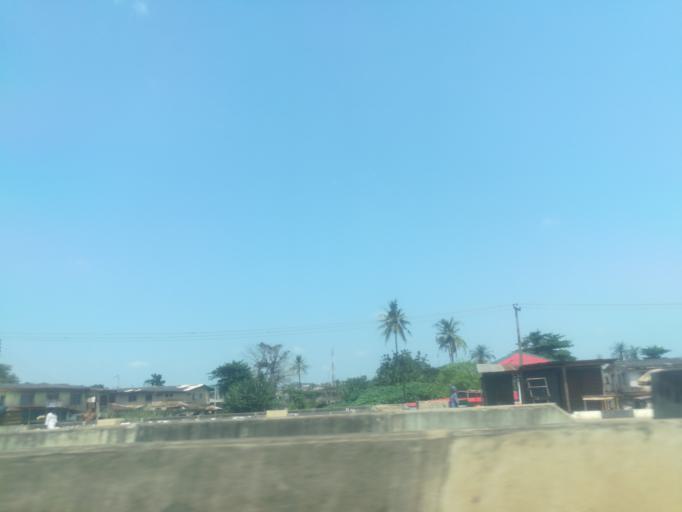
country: NG
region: Ogun
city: Abeokuta
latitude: 7.1487
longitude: 3.3593
